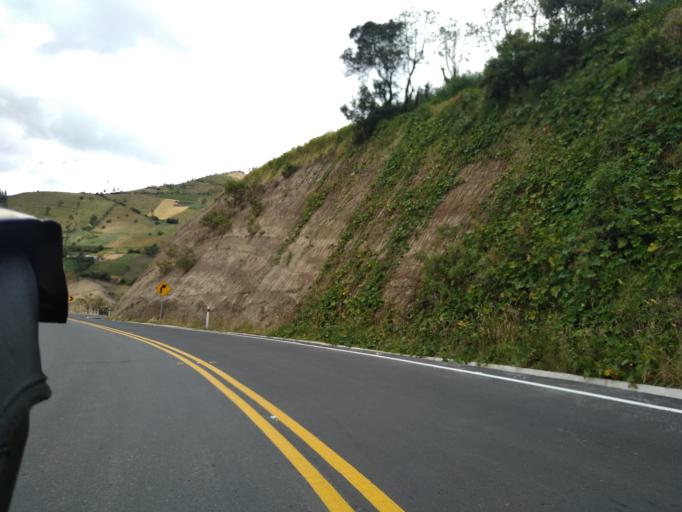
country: EC
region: Cotopaxi
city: Saquisili
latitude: -0.7631
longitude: -78.9102
